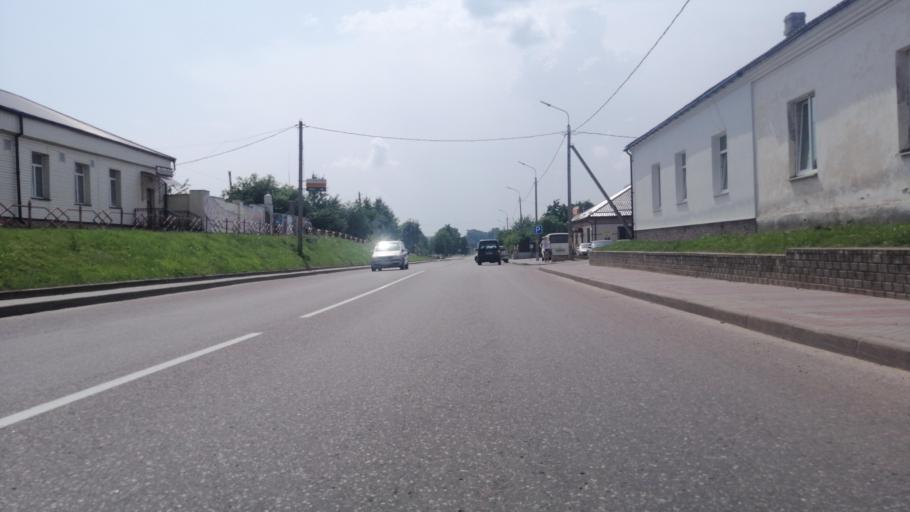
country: BY
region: Grodnenskaya
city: Navahrudak
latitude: 53.5886
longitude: 25.8129
